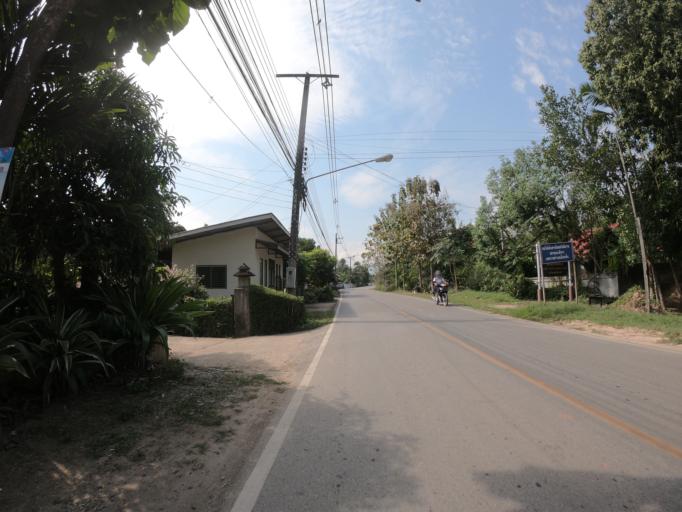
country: TH
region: Chiang Mai
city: San Sai
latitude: 18.8629
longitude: 99.0613
